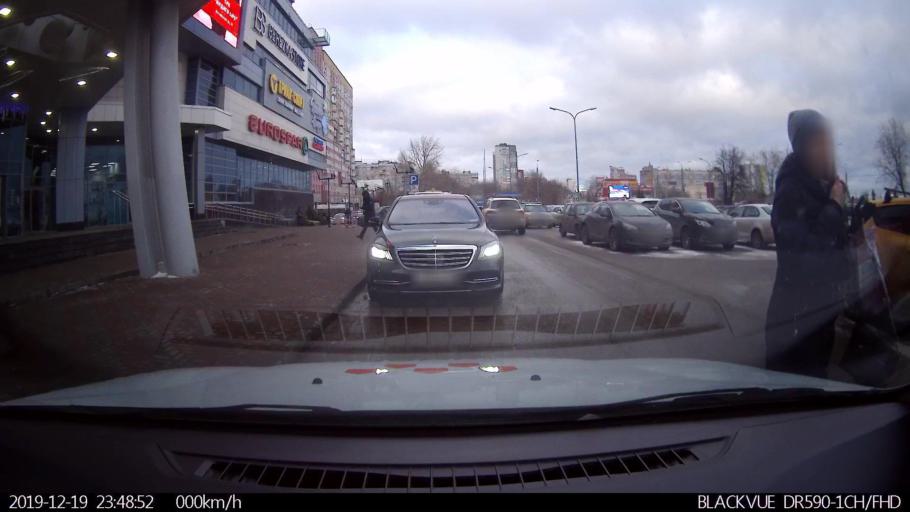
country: RU
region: Jaroslavl
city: Borok
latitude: 58.3105
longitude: 38.4419
